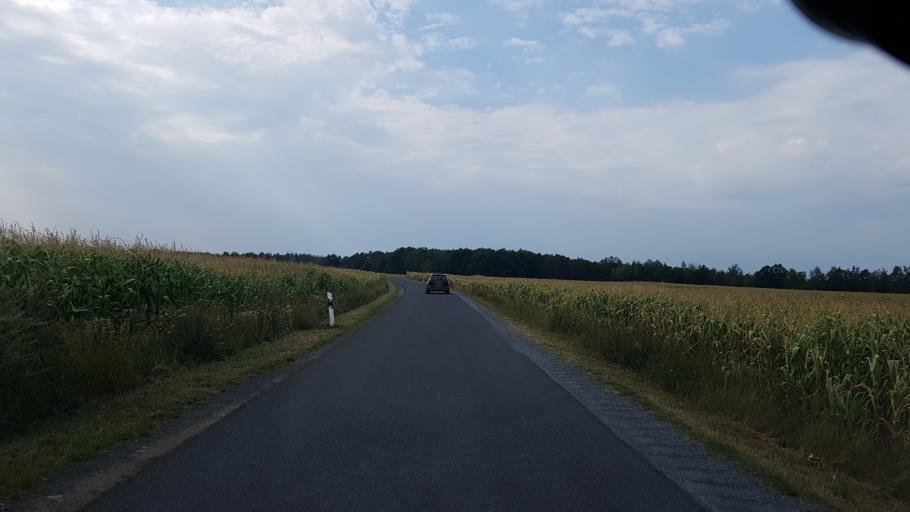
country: DE
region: Brandenburg
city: Lauchhammer
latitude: 51.5123
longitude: 13.6909
